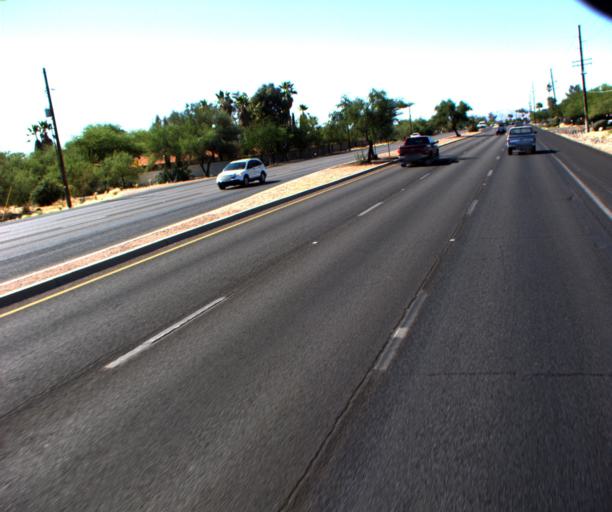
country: US
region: Arizona
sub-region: Pima County
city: Casas Adobes
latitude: 32.3278
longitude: -110.9759
